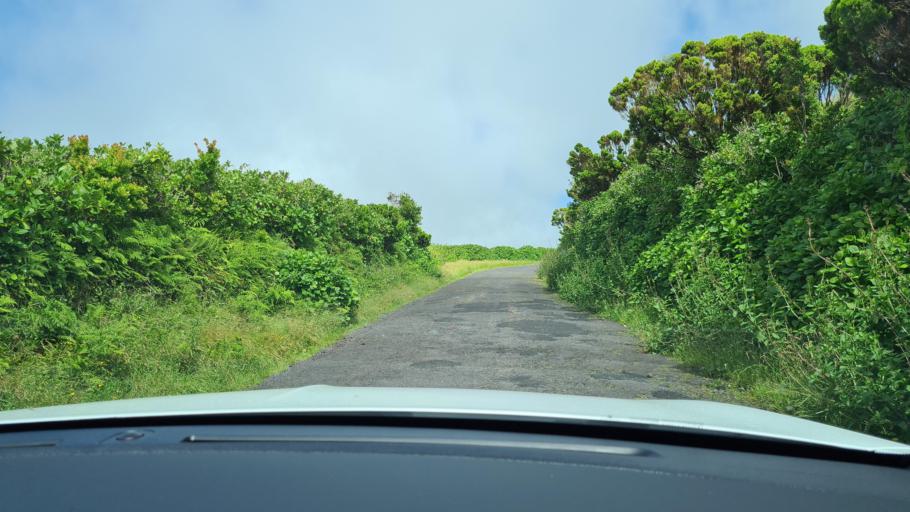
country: PT
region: Azores
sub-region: Sao Roque do Pico
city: Sao Roque do Pico
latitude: 38.6706
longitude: -28.1328
